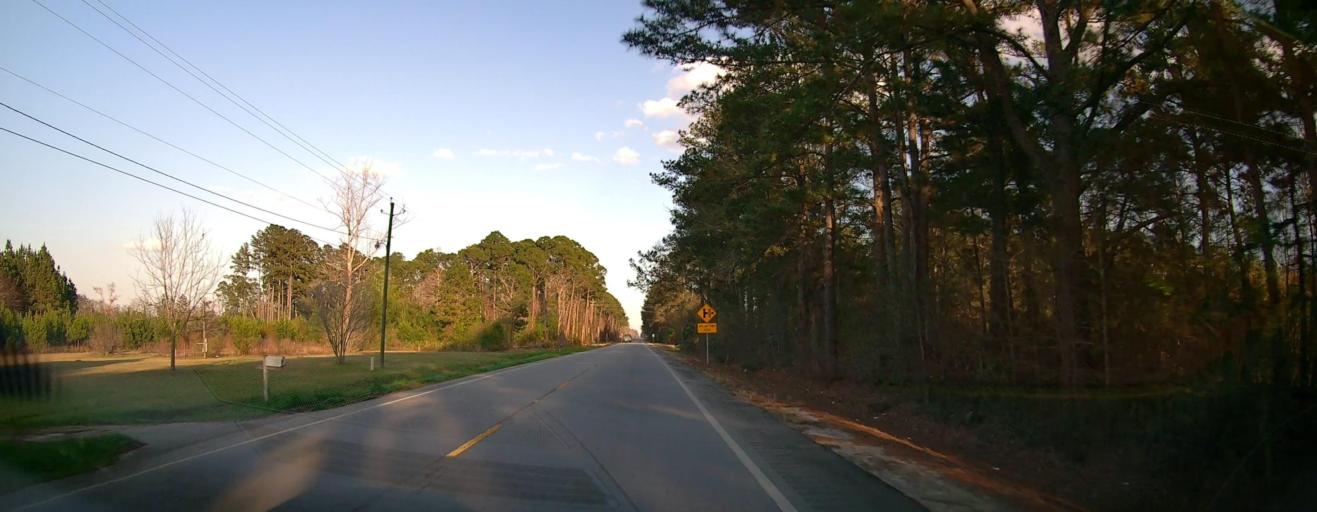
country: US
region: Georgia
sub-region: Bryan County
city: Pembroke
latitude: 32.1412
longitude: -81.7019
